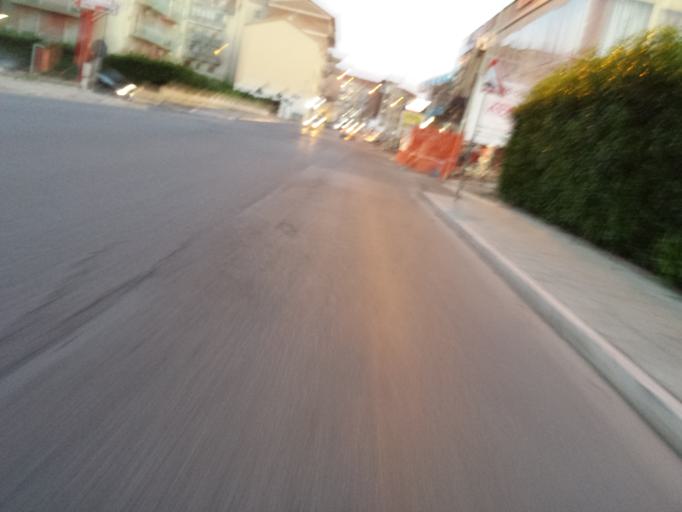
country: IT
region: Molise
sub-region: Provincia di Campobasso
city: Campobasso
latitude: 41.5708
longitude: 14.6748
